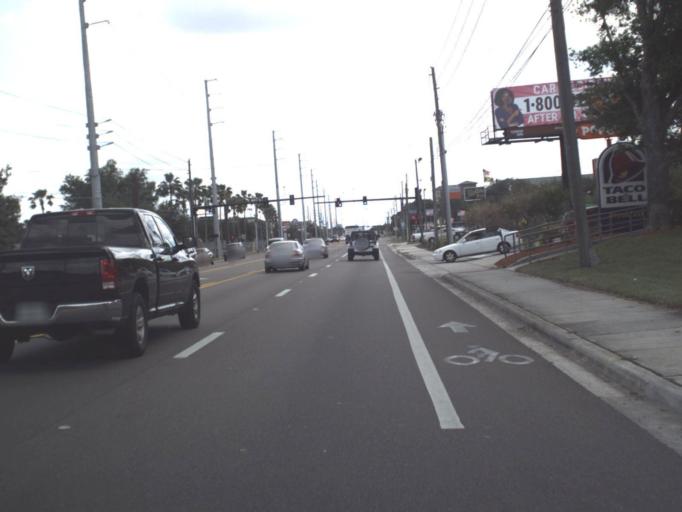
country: US
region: Florida
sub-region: Orange County
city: Belle Isle
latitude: 28.4509
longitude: -81.3607
